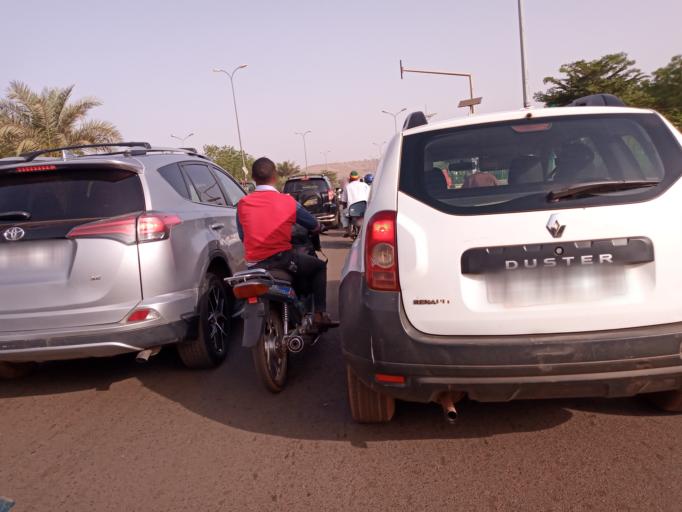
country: ML
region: Bamako
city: Bamako
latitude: 12.6403
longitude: -8.0064
